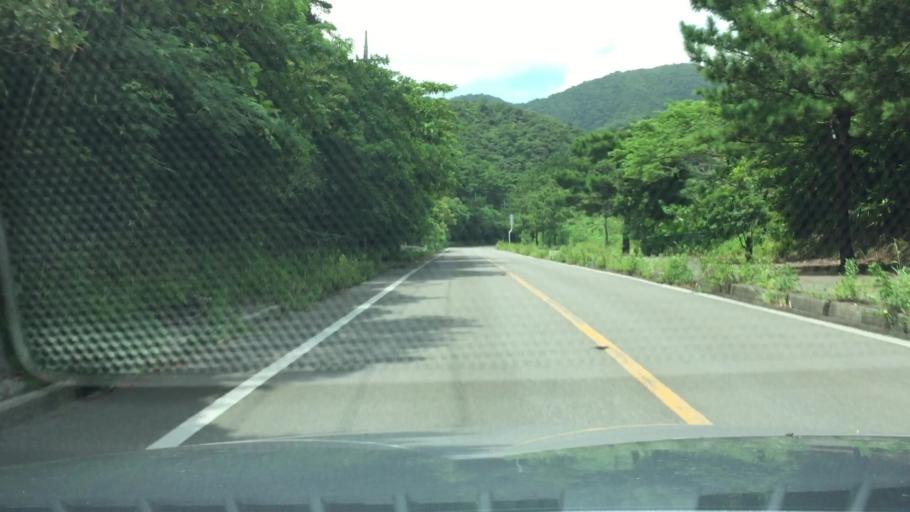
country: JP
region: Okinawa
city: Ishigaki
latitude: 24.4304
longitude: 124.2104
